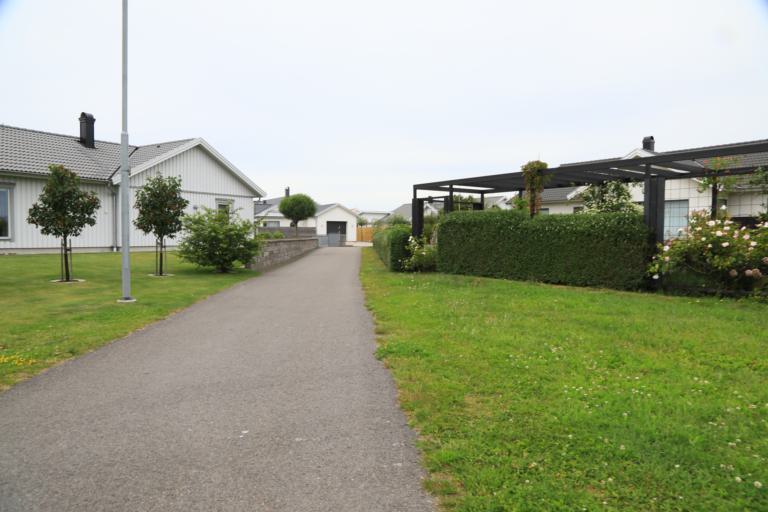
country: SE
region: Halland
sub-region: Varbergs Kommun
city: Traslovslage
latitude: 57.0845
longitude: 12.2817
